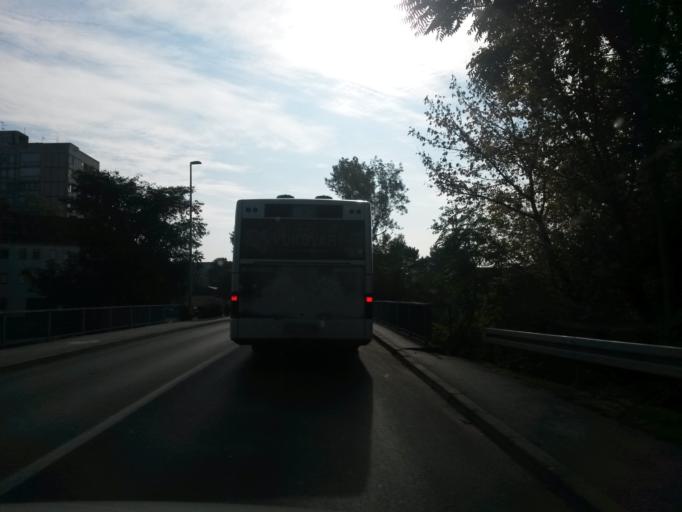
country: HR
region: Vukovarsko-Srijemska
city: Vukovar
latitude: 45.3607
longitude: 18.9892
